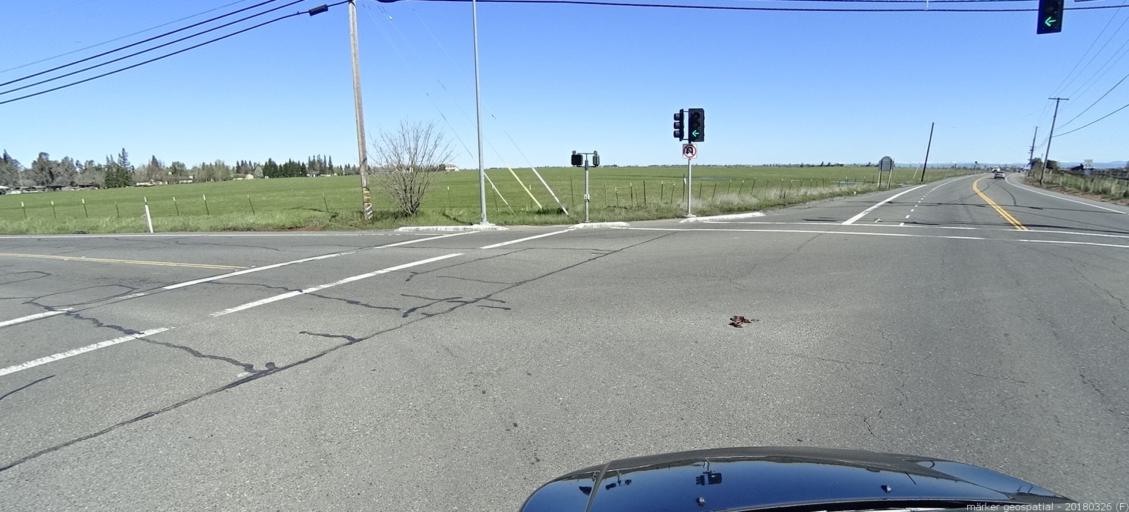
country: US
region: California
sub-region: Sacramento County
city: Wilton
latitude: 38.4525
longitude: -121.2771
